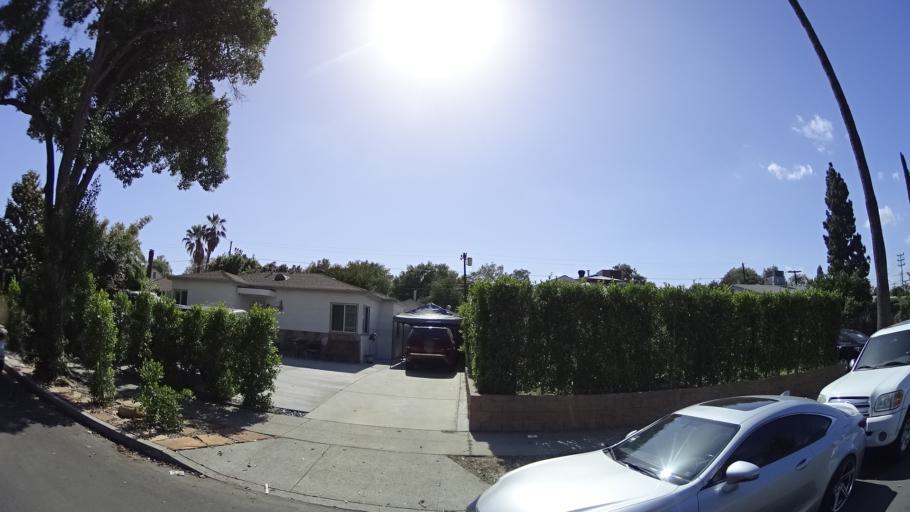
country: US
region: California
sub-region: Los Angeles County
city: North Hollywood
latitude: 34.1772
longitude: -118.3648
